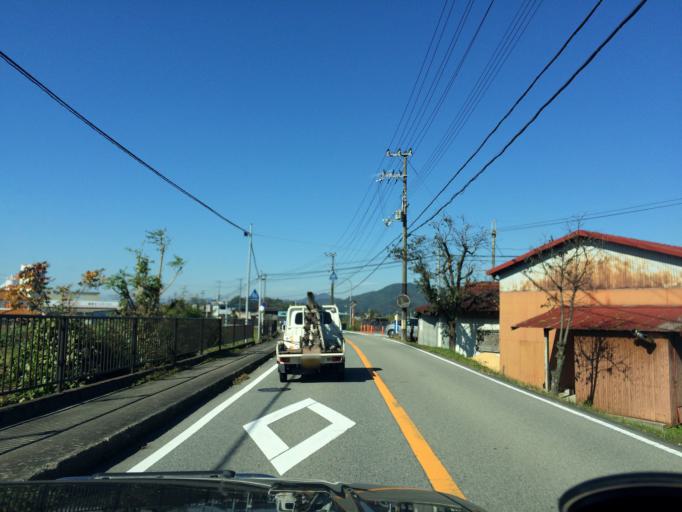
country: JP
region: Hyogo
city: Sasayama
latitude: 35.0666
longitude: 135.2437
